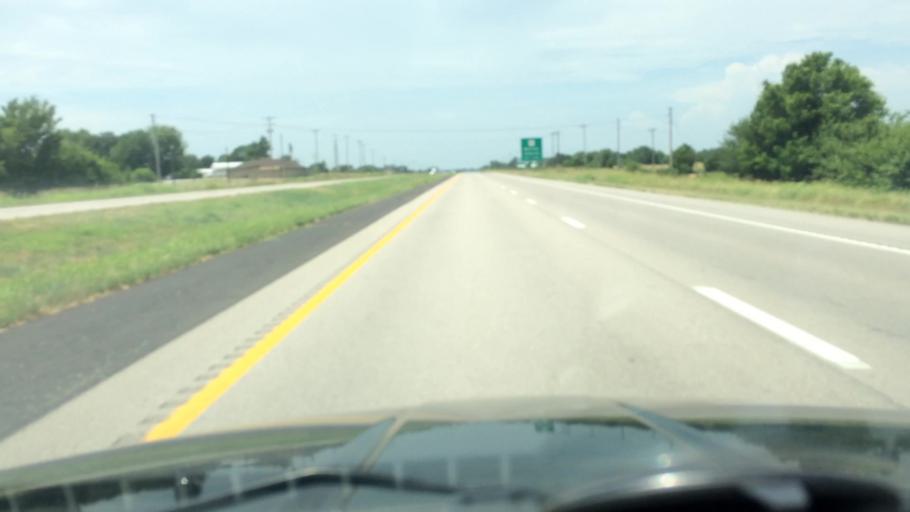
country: US
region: Missouri
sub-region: Polk County
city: Bolivar
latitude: 37.5817
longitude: -93.4093
